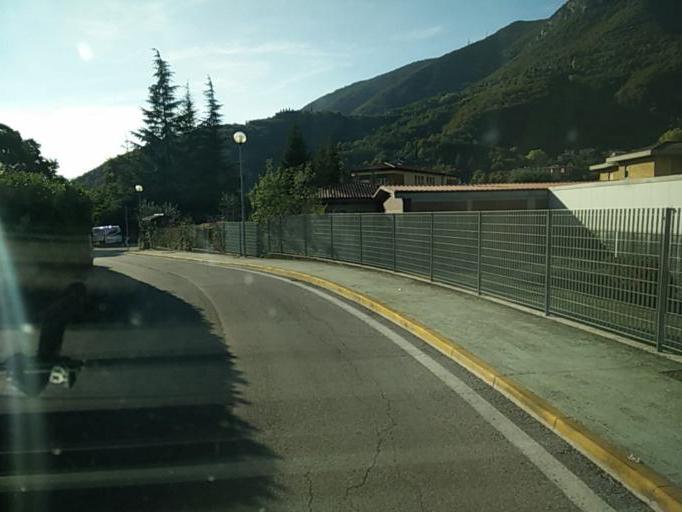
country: IT
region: Lombardy
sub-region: Provincia di Brescia
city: Roe Volciano
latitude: 45.6148
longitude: 10.4865
